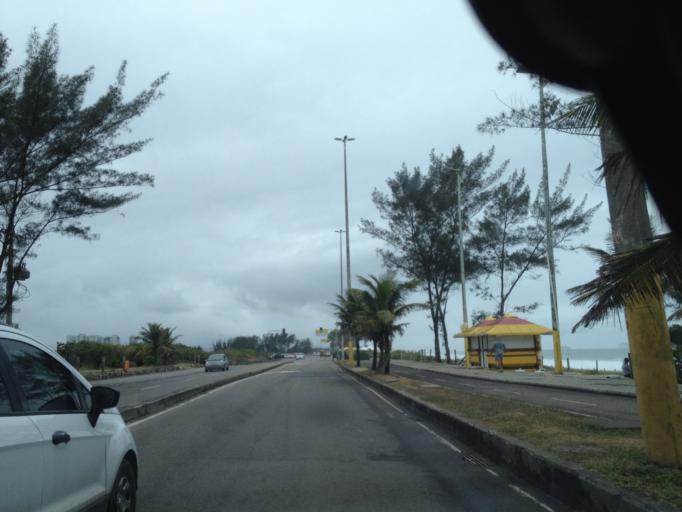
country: BR
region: Rio de Janeiro
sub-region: Nilopolis
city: Nilopolis
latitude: -23.0210
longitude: -43.4412
